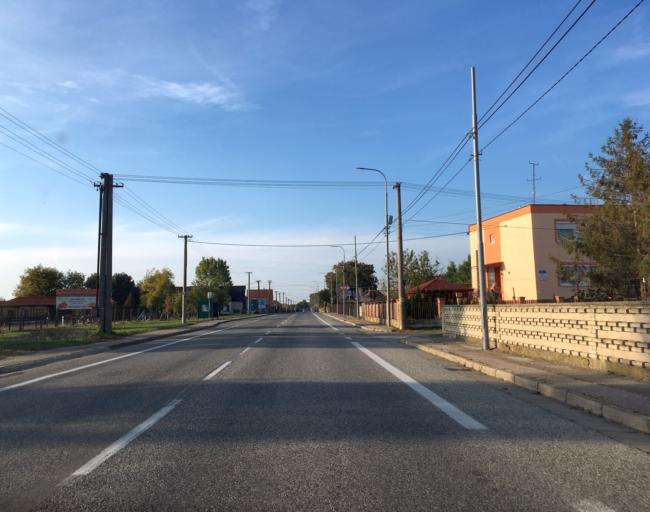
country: SK
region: Nitriansky
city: Surany
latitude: 48.0870
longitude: 18.0707
